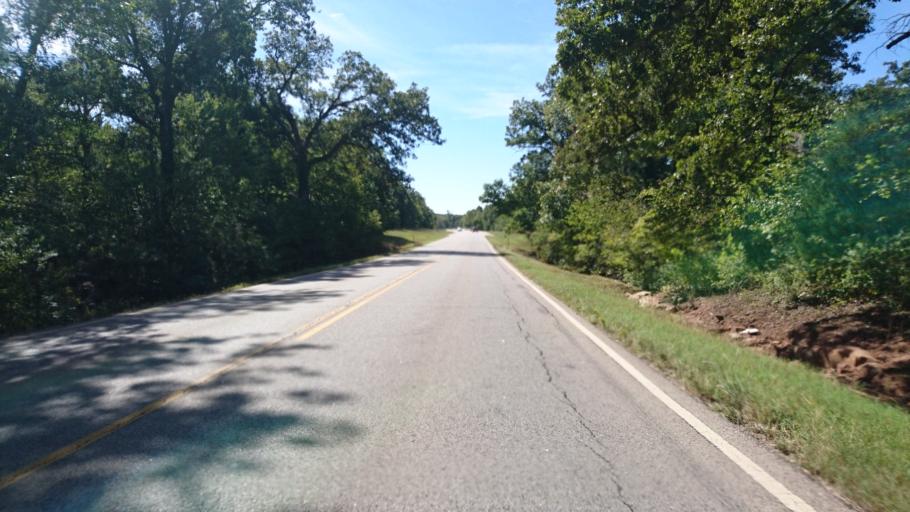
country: US
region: Oklahoma
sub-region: Lincoln County
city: Stroud
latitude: 35.7391
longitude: -96.7132
